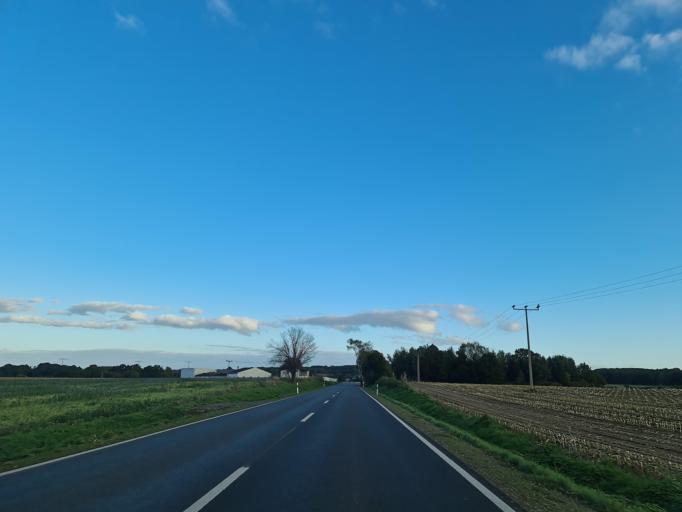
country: DE
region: Thuringia
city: Hohenolsen
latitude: 50.7327
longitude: 12.0964
